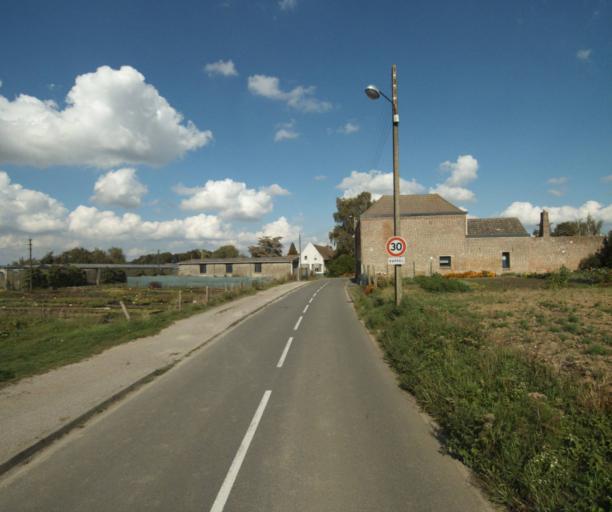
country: FR
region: Nord-Pas-de-Calais
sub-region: Departement du Nord
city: Herlies
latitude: 50.5683
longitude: 2.8634
